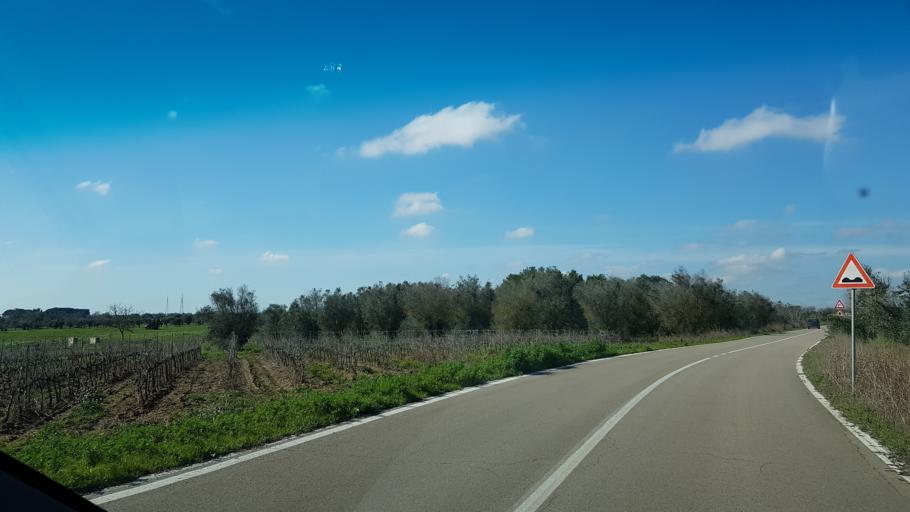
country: IT
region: Apulia
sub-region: Provincia di Brindisi
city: Cellino San Marco
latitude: 40.4395
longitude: 17.9942
